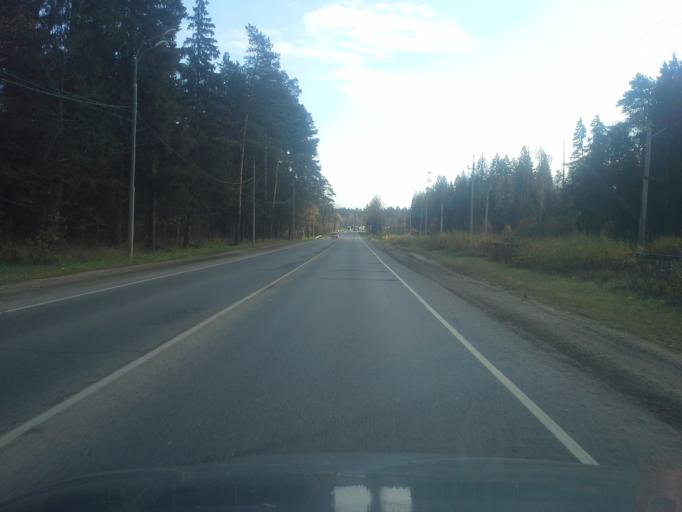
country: RU
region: Moskovskaya
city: Bol'shiye Vyazemy
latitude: 55.6734
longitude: 36.9397
